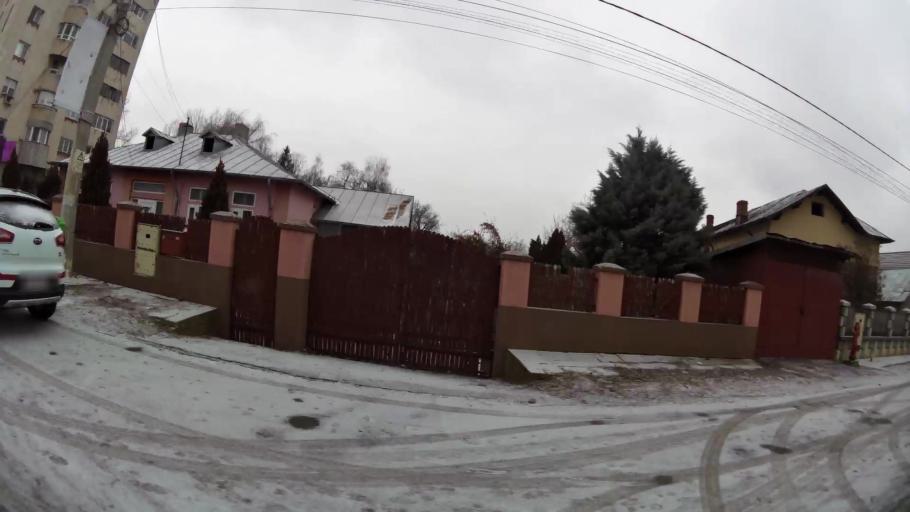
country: RO
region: Dambovita
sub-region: Comuna Ulmi
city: Ulmi
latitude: 44.9171
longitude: 25.4822
